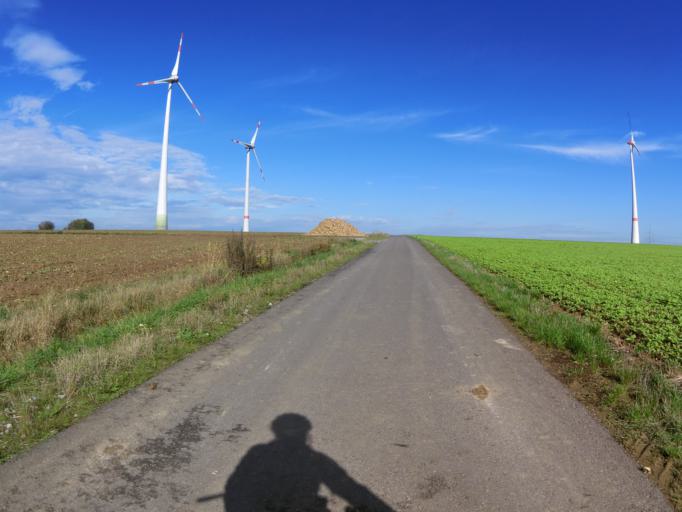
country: DE
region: Bavaria
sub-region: Regierungsbezirk Unterfranken
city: Sommerhausen
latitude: 49.7148
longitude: 10.0463
